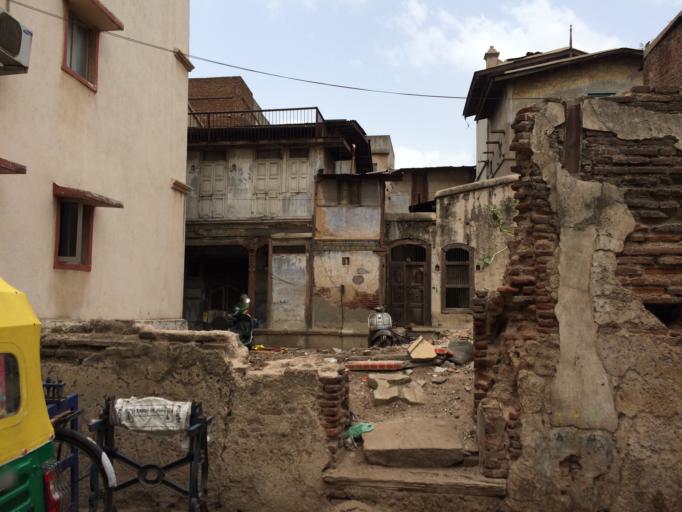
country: IN
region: Gujarat
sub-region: Ahmadabad
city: Ahmedabad
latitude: 23.0187
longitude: 72.5961
